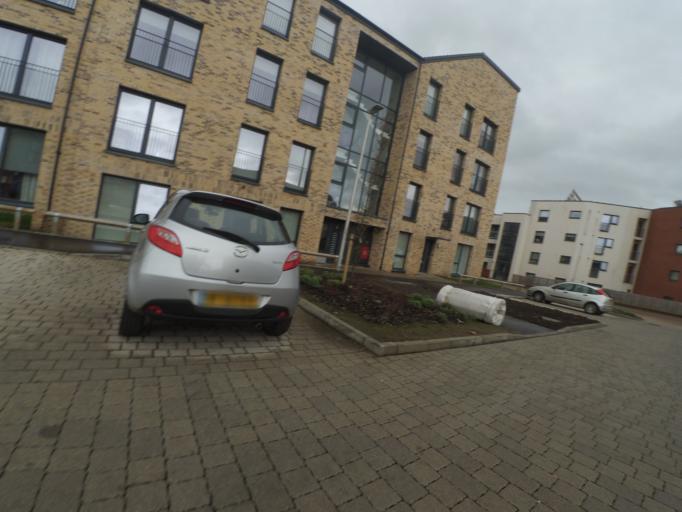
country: GB
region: Scotland
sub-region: West Lothian
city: Seafield
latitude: 55.9338
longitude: -3.1310
